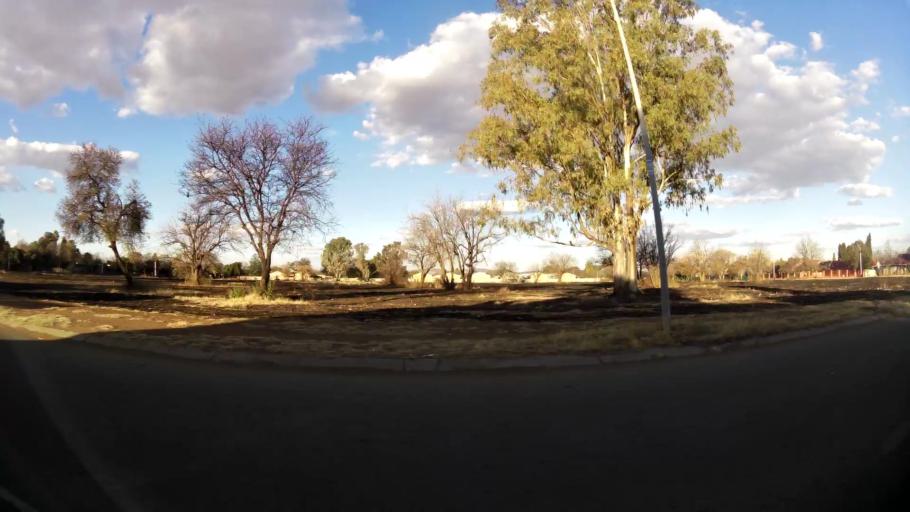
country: ZA
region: North-West
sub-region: Dr Kenneth Kaunda District Municipality
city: Potchefstroom
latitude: -26.7361
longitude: 27.0952
